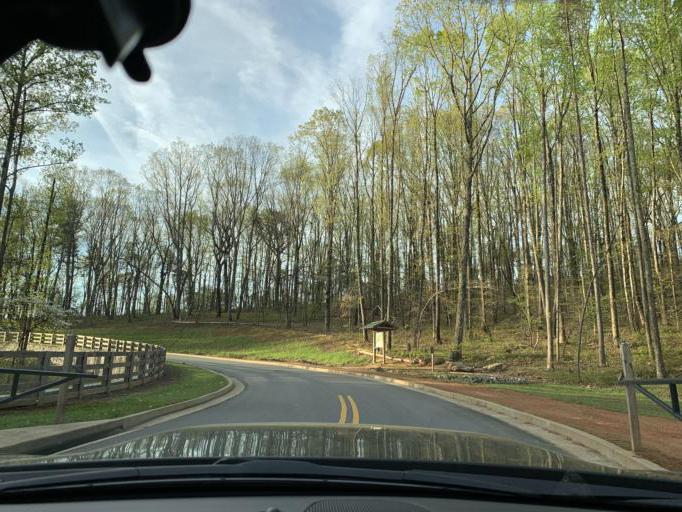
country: US
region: Georgia
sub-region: Forsyth County
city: Cumming
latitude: 34.2437
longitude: -84.1396
